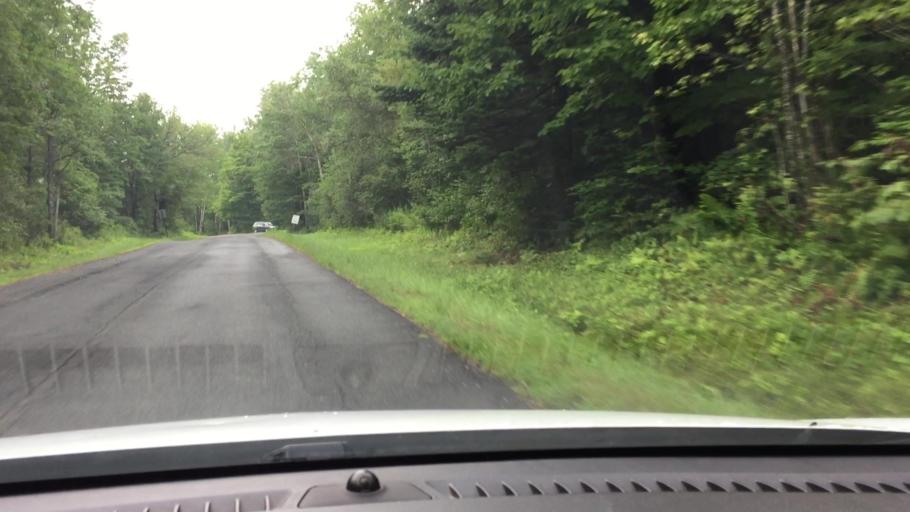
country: US
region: Massachusetts
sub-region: Berkshire County
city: Hinsdale
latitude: 42.4144
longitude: -73.0560
